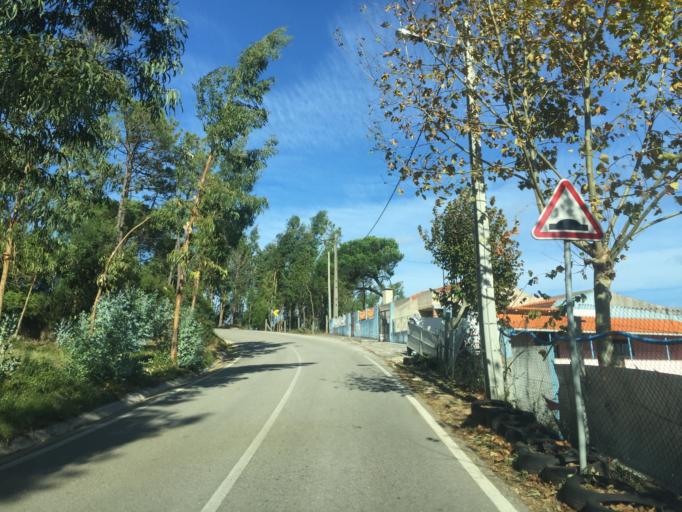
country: PT
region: Coimbra
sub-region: Figueira da Foz
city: Tavarede
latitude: 40.1777
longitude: -8.8376
